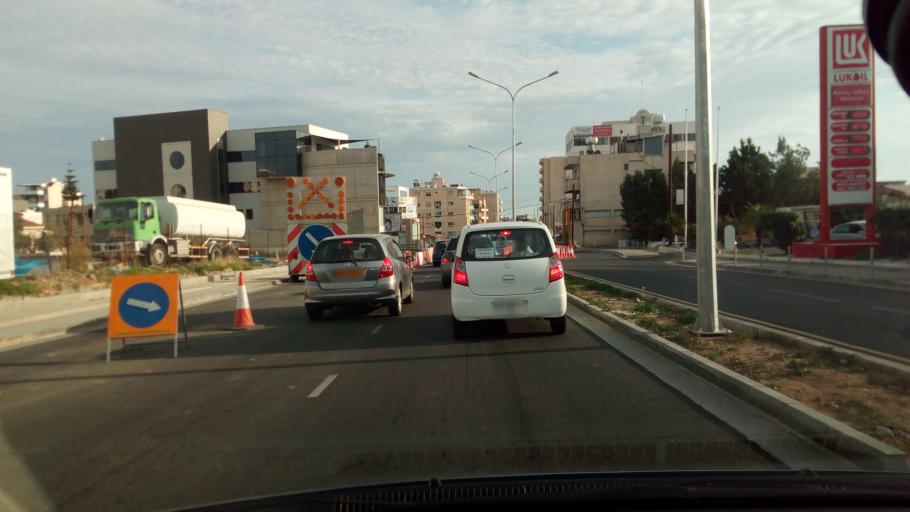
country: CY
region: Limassol
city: Limassol
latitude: 34.7002
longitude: 33.0307
